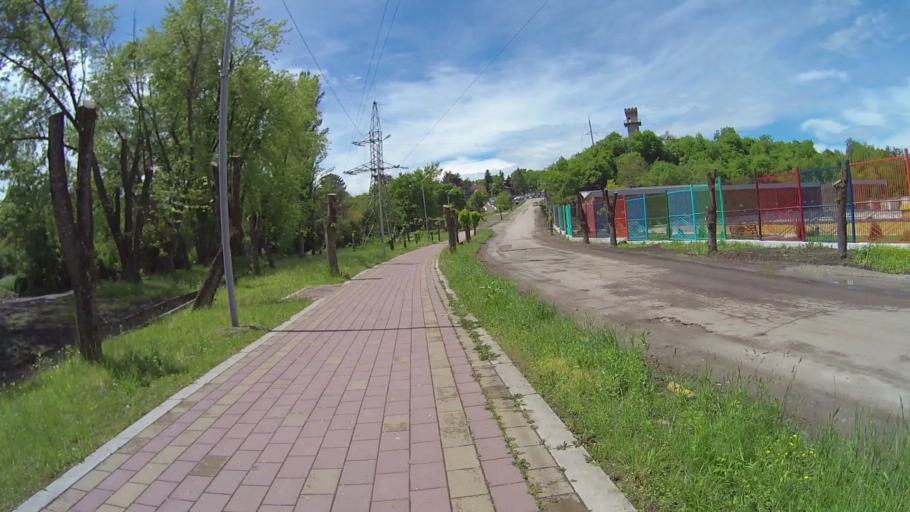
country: RU
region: Kabardino-Balkariya
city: Vol'nyy Aul
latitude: 43.4589
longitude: 43.5915
